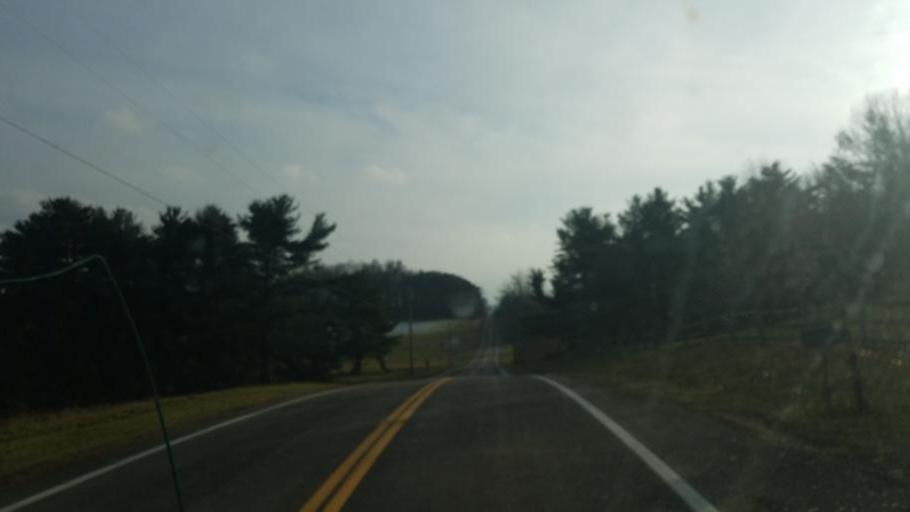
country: US
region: Ohio
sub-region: Sandusky County
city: Bellville
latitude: 40.6651
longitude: -82.3776
